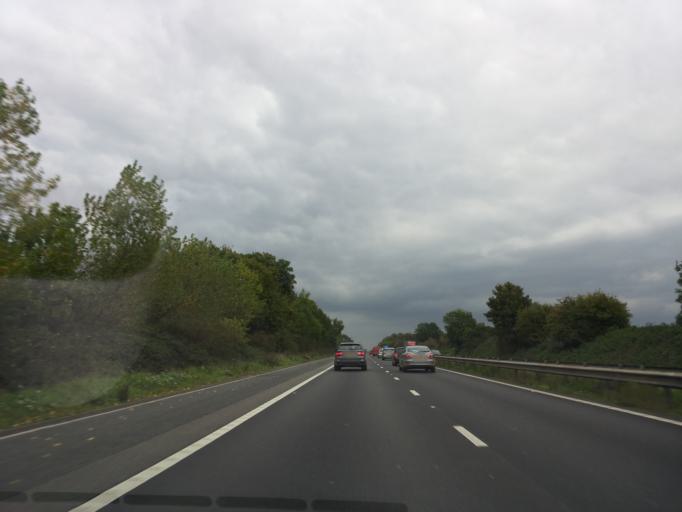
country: GB
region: England
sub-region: Kent
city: Newington
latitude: 51.3353
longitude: 0.6483
